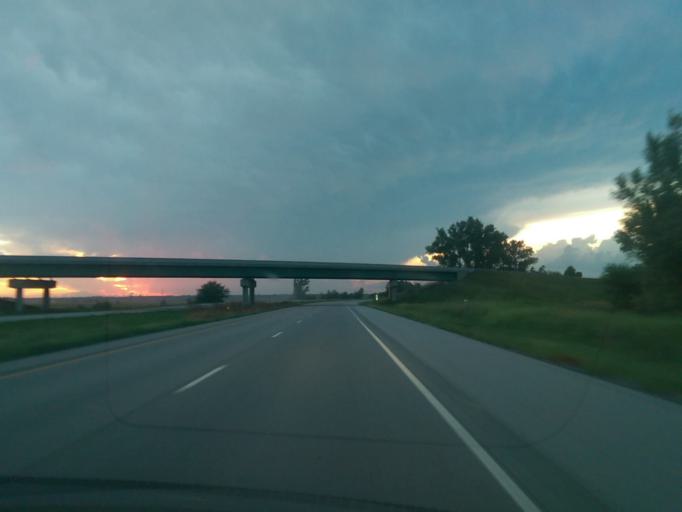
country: US
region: Nebraska
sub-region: Otoe County
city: Nebraska City
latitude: 40.7230
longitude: -95.8113
